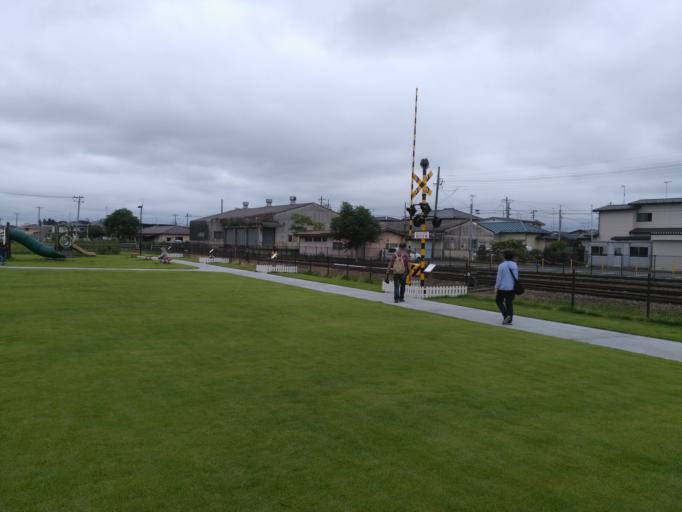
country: JP
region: Iwate
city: Ichinoseki
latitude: 38.7751
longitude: 141.1333
